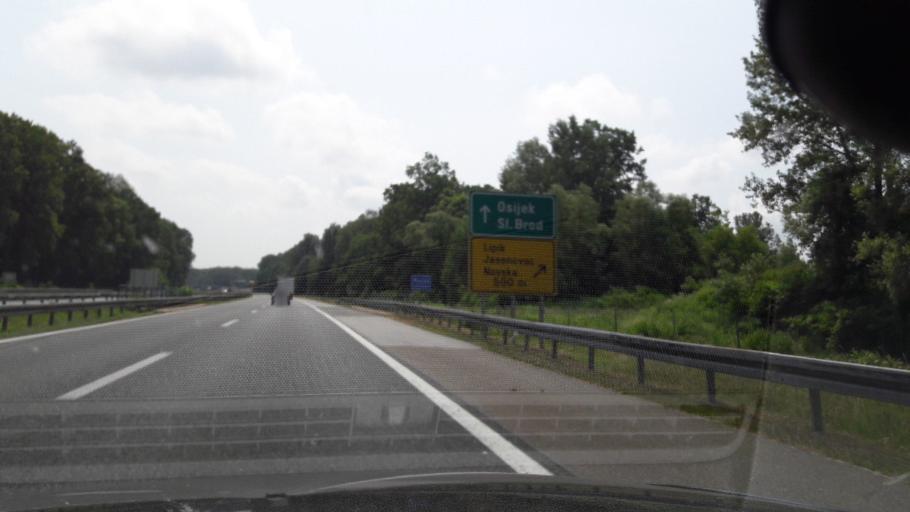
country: HR
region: Sisacko-Moslavacka
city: Novska
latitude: 45.3339
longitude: 16.9316
